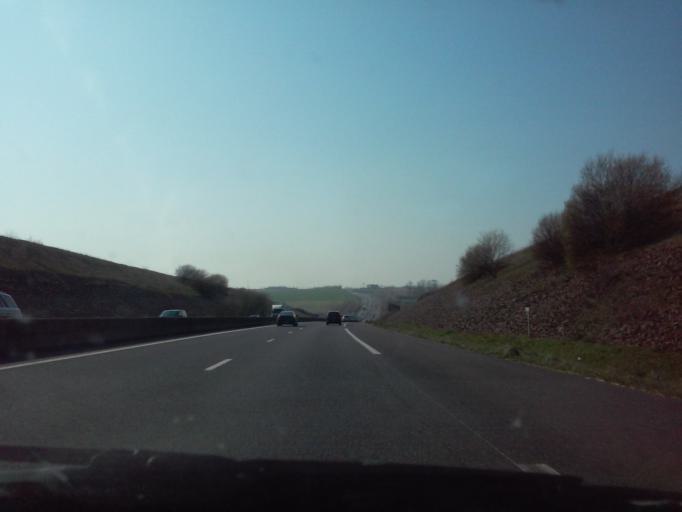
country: FR
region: Lower Normandy
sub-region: Departement du Calvados
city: Saint-Vigor-le-Grand
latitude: 49.2484
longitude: -0.6276
